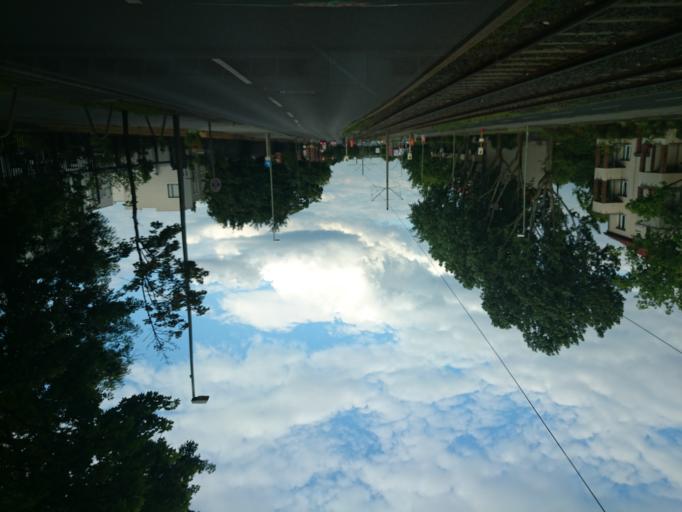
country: DE
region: Berlin
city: Rummelsburg
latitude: 52.4977
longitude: 13.4834
